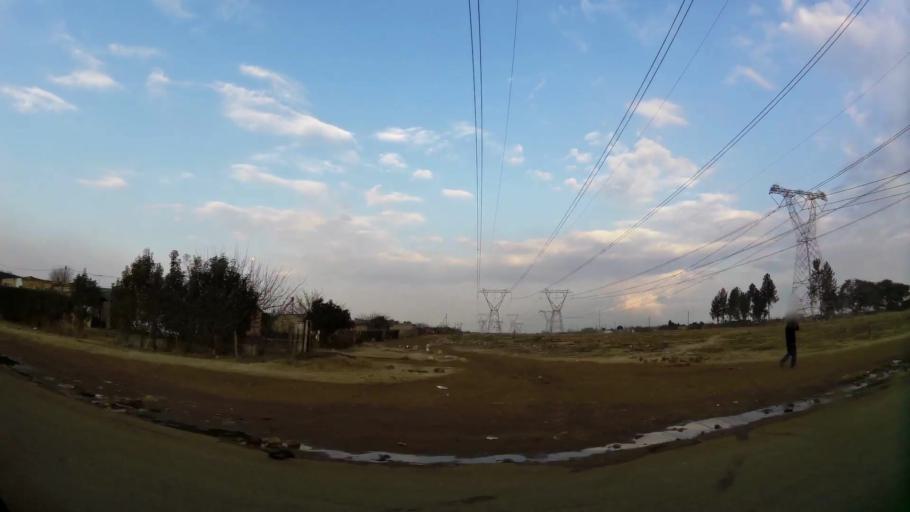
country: ZA
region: Gauteng
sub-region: City of Johannesburg Metropolitan Municipality
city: Orange Farm
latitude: -26.5521
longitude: 27.8316
